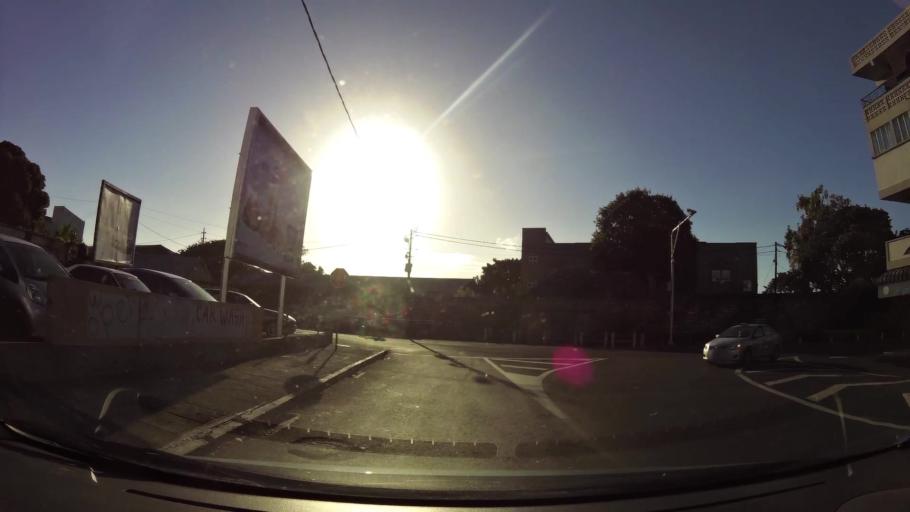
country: MU
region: Port Louis
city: Port Louis
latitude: -20.1670
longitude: 57.4988
